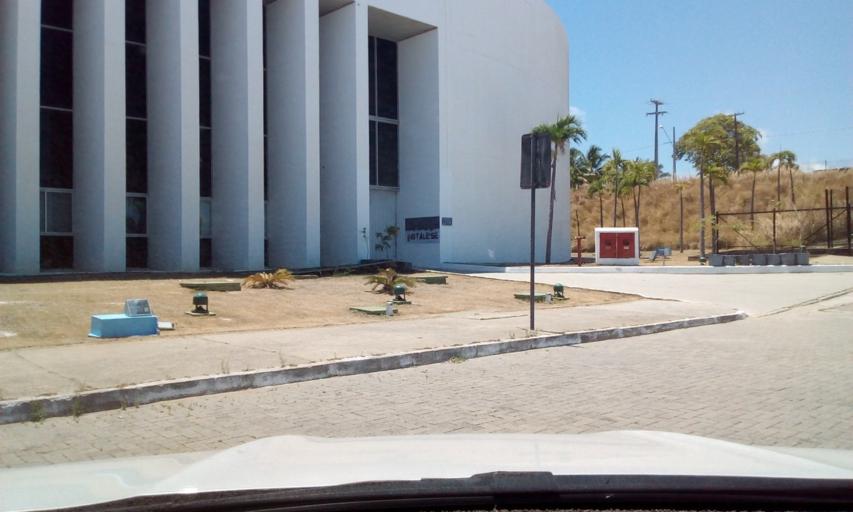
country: BR
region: Paraiba
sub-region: Joao Pessoa
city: Joao Pessoa
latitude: -7.1510
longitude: -34.7981
